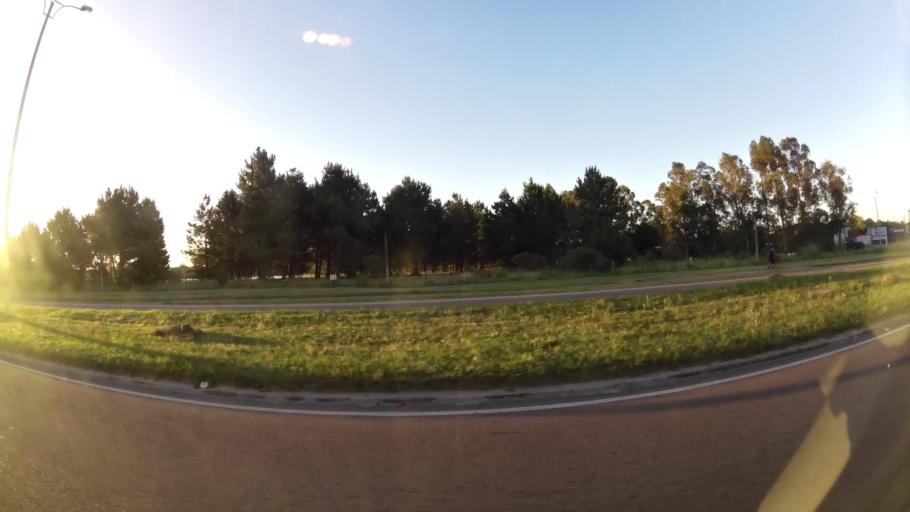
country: UY
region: Canelones
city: Barra de Carrasco
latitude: -34.8442
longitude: -55.9993
